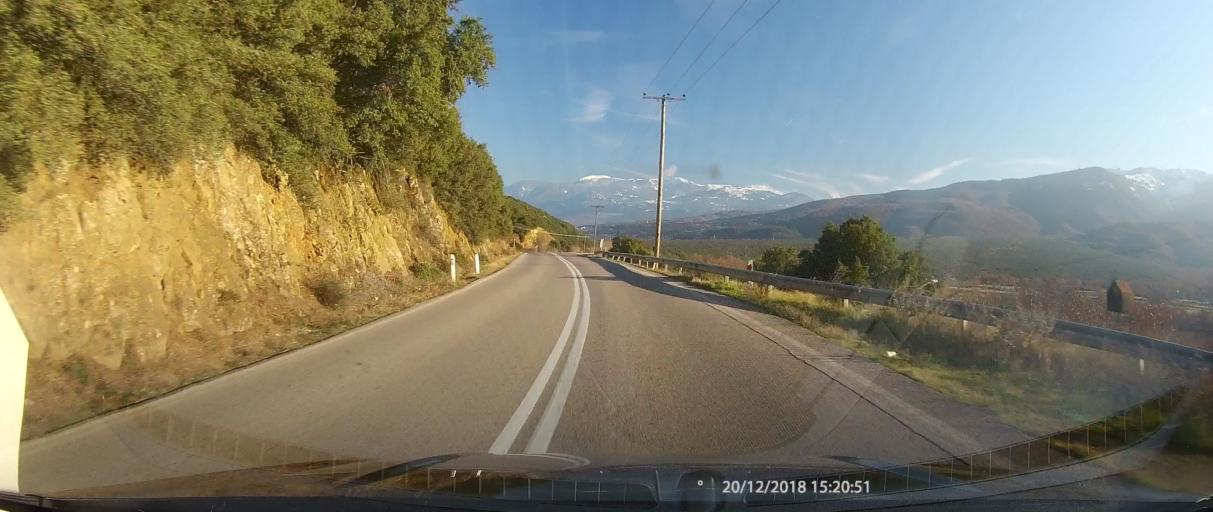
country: GR
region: Central Greece
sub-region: Nomos Fthiotidos
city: Makrakomi
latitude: 38.9324
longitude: 22.0641
